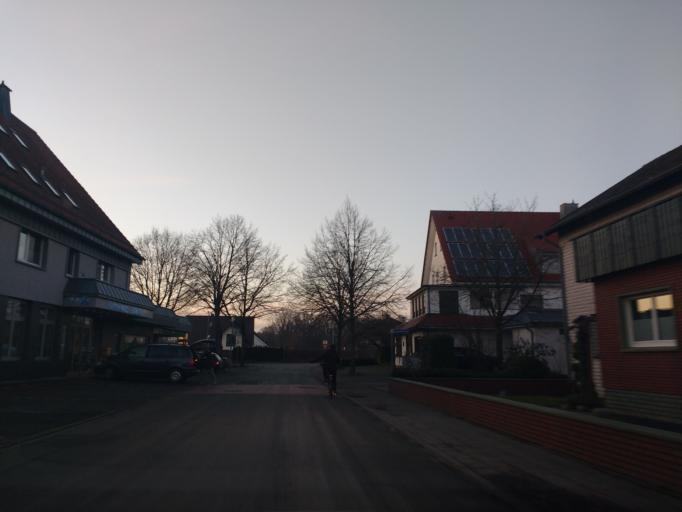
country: DE
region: North Rhine-Westphalia
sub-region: Regierungsbezirk Detmold
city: Hovelhof
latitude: 51.8496
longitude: 8.6245
